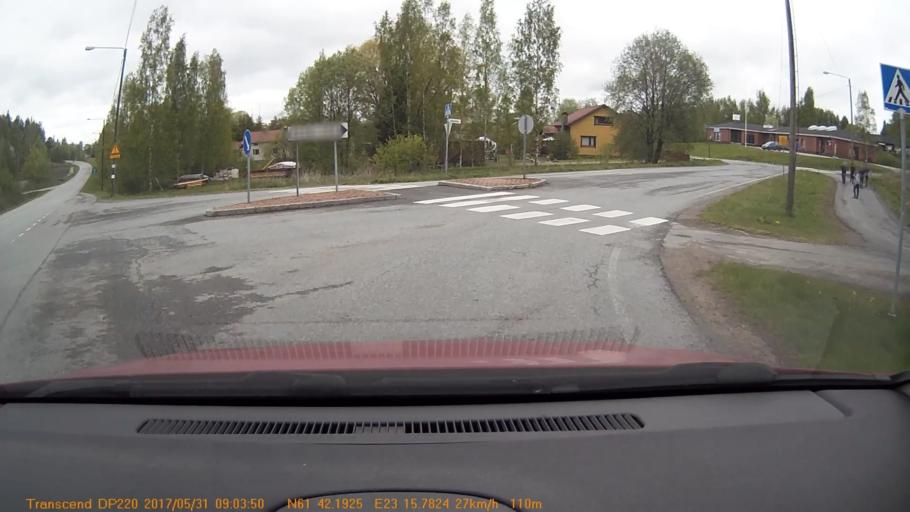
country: FI
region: Pirkanmaa
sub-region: Tampere
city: Viljakkala
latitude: 61.7032
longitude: 23.2635
